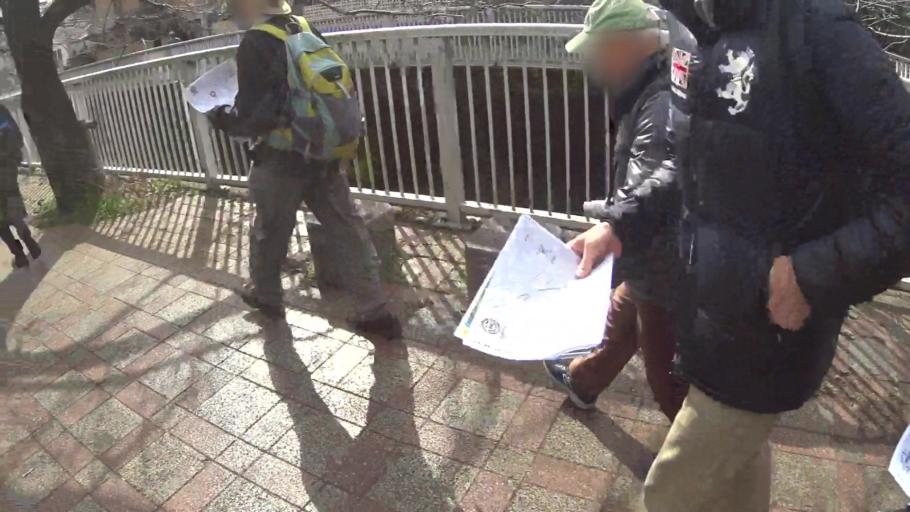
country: JP
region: Tokyo
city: Mitaka-shi
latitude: 35.6901
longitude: 139.5932
